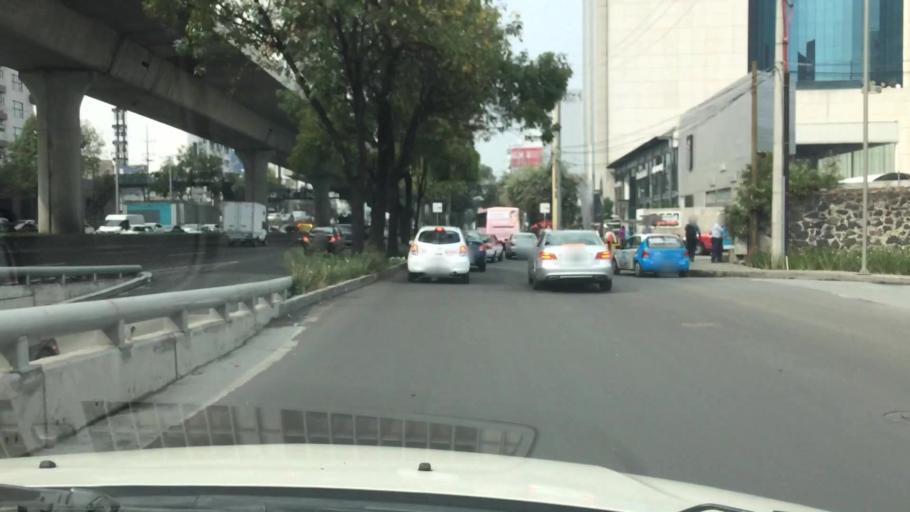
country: MX
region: Mexico City
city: Magdalena Contreras
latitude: 19.3149
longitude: -99.2206
